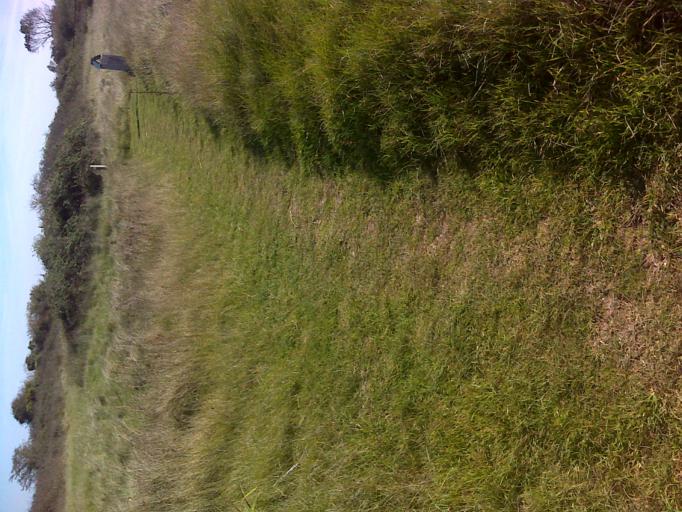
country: FR
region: Poitou-Charentes
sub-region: Departement de la Charente-Maritime
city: Port-des-Barques
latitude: 45.9004
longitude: -1.0712
